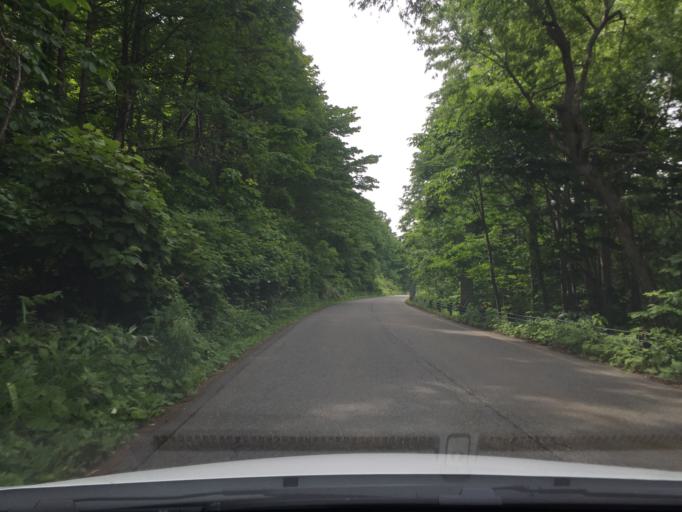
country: JP
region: Fukushima
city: Inawashiro
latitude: 37.6419
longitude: 140.0412
